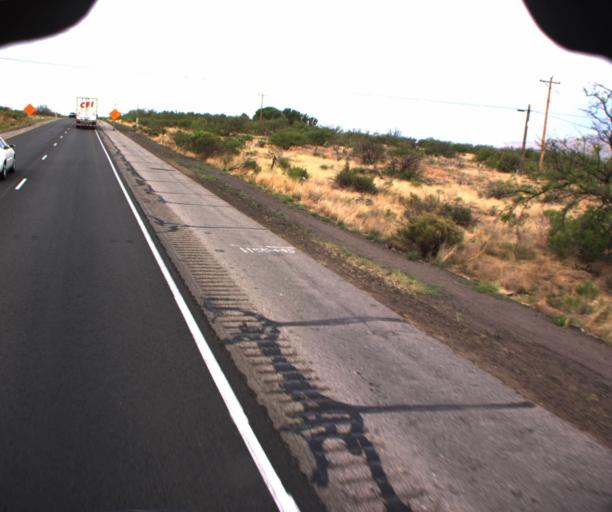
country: US
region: Arizona
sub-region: Cochise County
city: Whetstone
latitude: 31.9633
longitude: -110.3829
